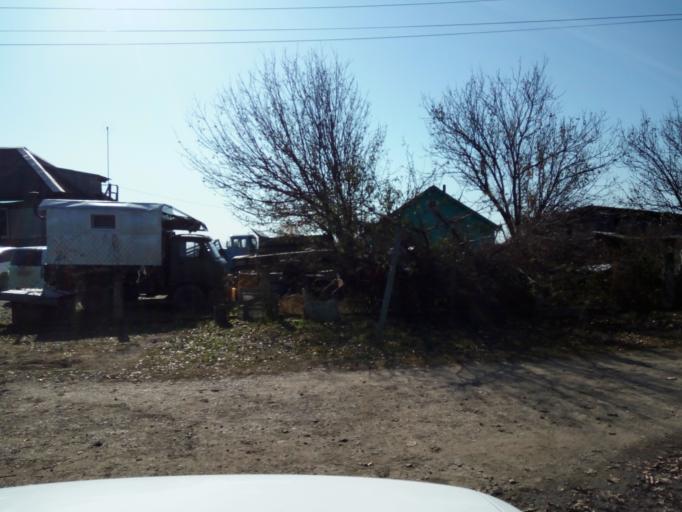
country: RU
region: Primorskiy
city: Dal'nerechensk
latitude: 45.9072
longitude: 133.7913
